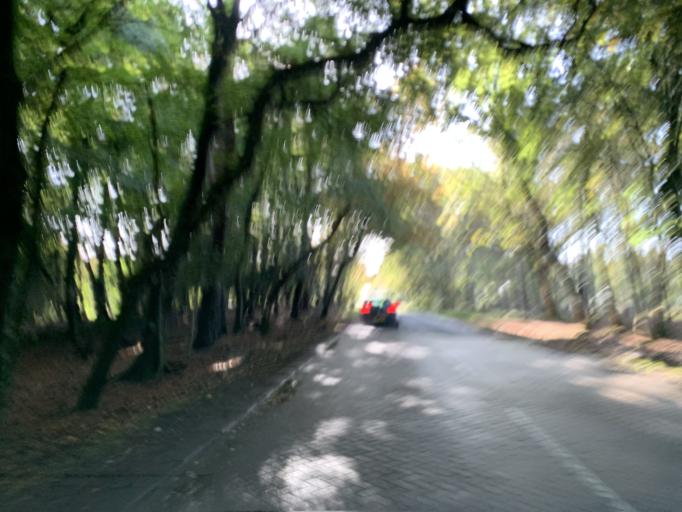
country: GB
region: England
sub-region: Wiltshire
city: Downton
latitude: 50.9637
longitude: -1.7021
